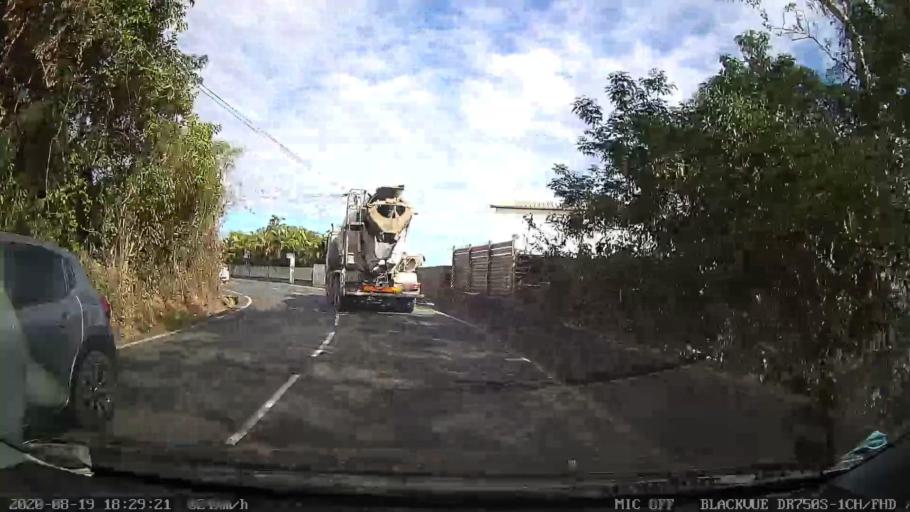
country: RE
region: Reunion
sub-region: Reunion
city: La Possession
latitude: -20.9576
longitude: 55.3490
